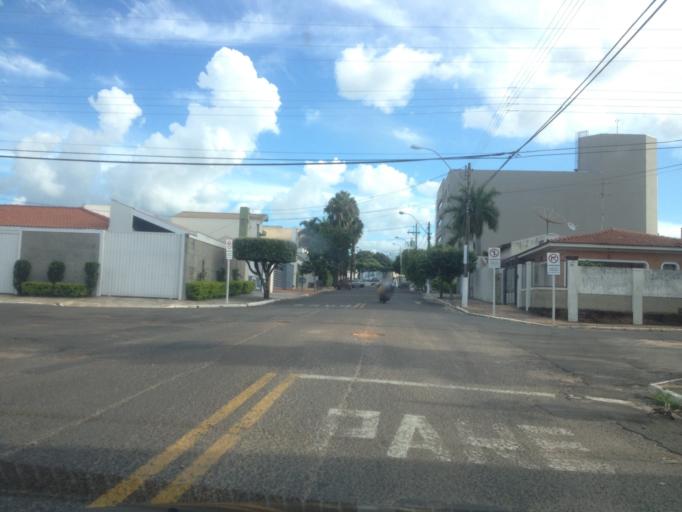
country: BR
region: Sao Paulo
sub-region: Marilia
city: Marilia
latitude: -22.2238
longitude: -49.9324
